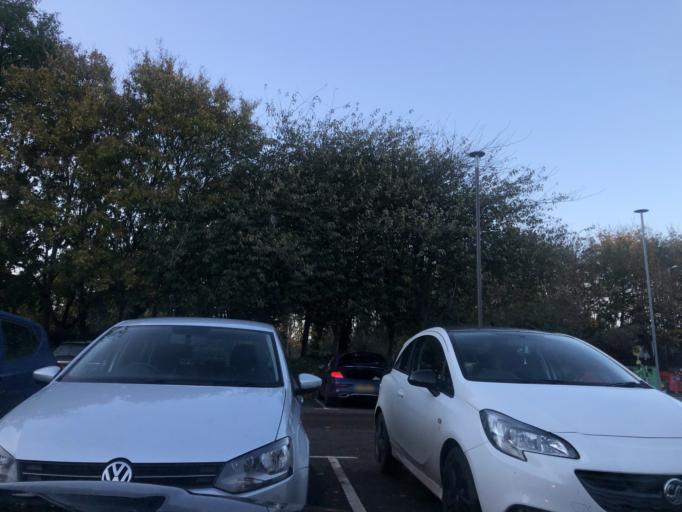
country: GB
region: England
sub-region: Oxfordshire
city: Banbury
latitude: 52.0508
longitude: -1.3347
